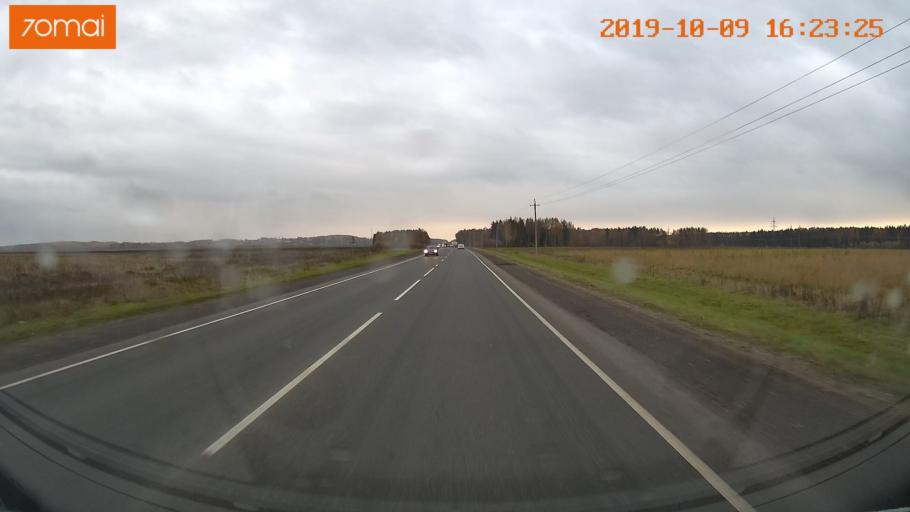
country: RU
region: Kostroma
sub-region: Kostromskoy Rayon
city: Kostroma
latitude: 57.6644
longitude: 40.8987
